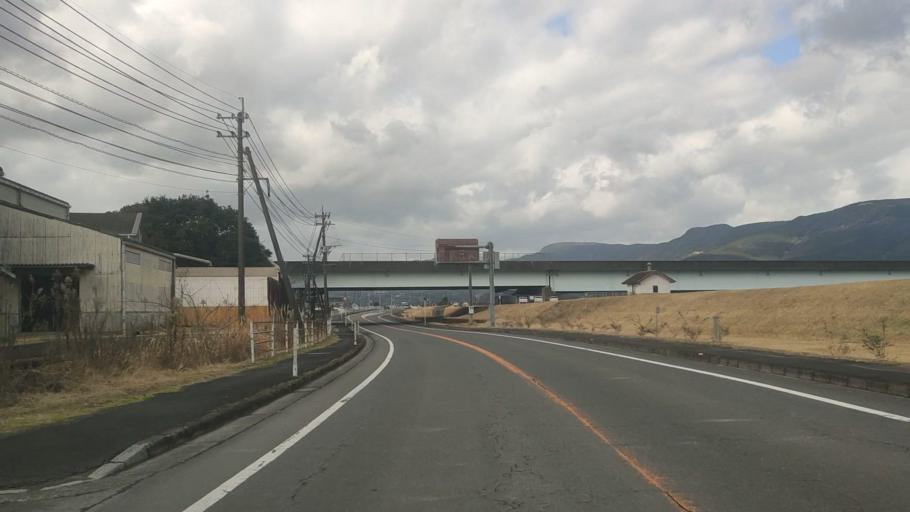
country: JP
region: Kumamoto
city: Hitoyoshi
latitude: 32.0528
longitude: 130.8031
